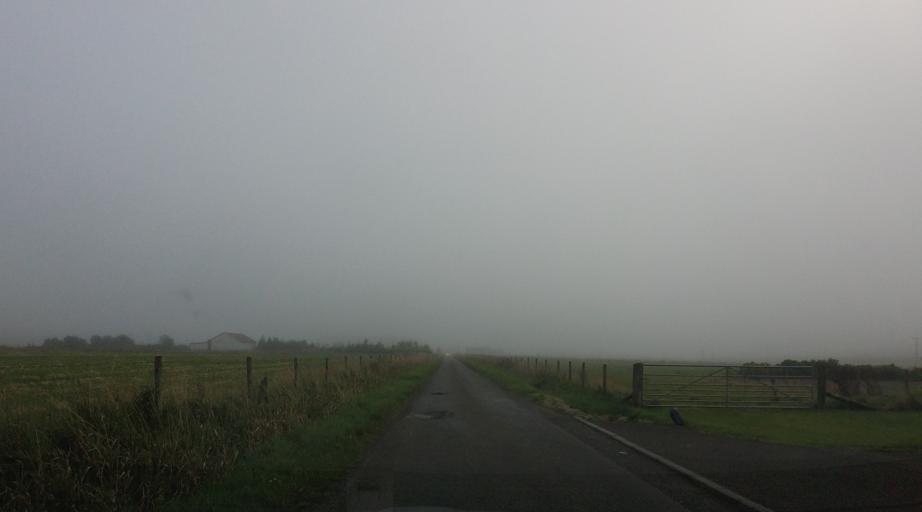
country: GB
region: Scotland
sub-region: Highland
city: Wick
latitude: 58.3194
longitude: -3.3014
